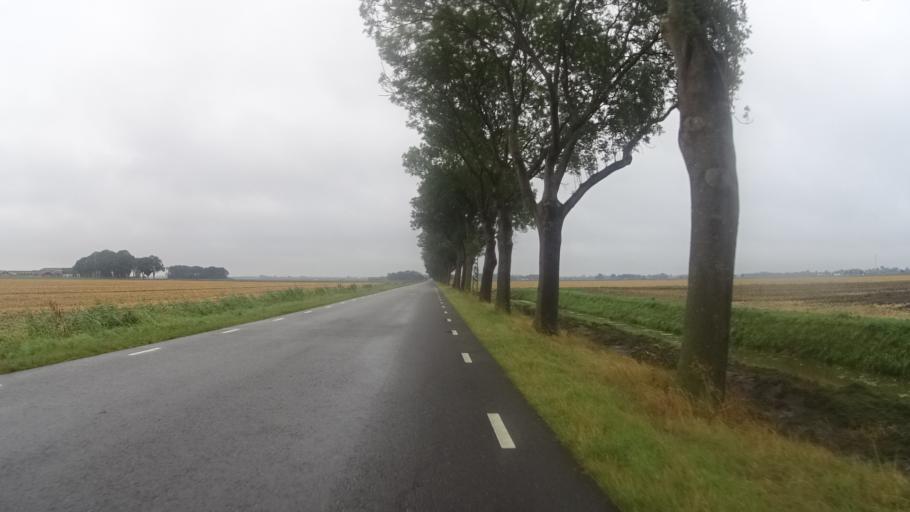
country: NL
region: Groningen
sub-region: Gemeente Veendam
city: Veendam
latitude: 53.1899
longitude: 6.9266
